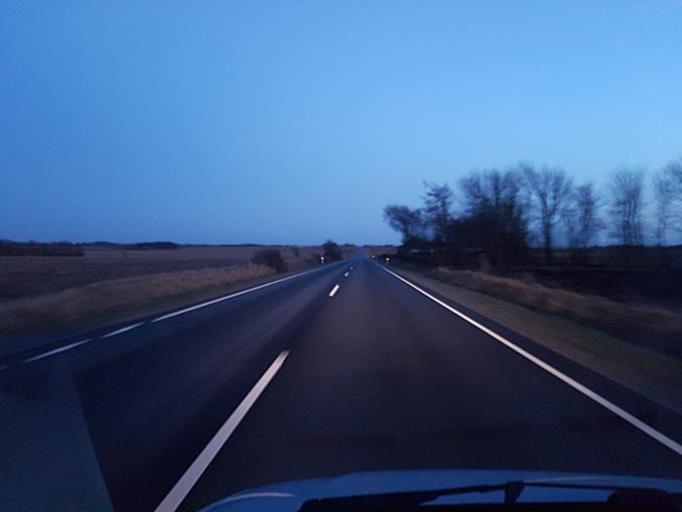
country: DK
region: Central Jutland
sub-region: Ringkobing-Skjern Kommune
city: Skjern
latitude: 56.0105
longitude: 8.5030
